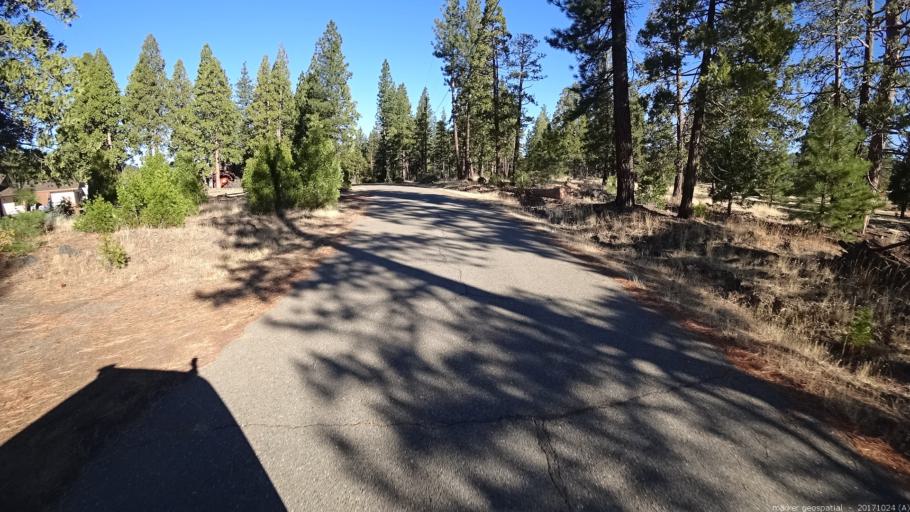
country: US
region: California
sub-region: Shasta County
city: Burney
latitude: 40.8370
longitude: -121.5139
